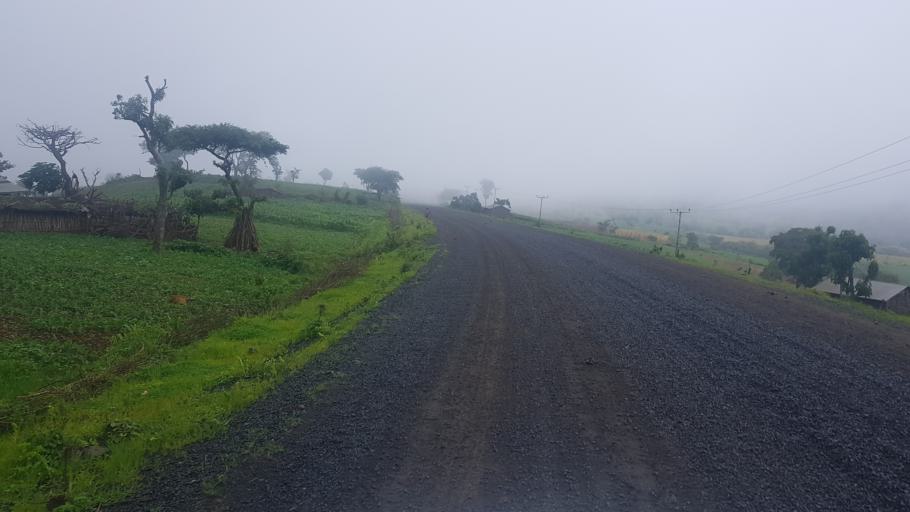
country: ET
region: Amhara
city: Bure
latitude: 10.1958
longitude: 36.9754
